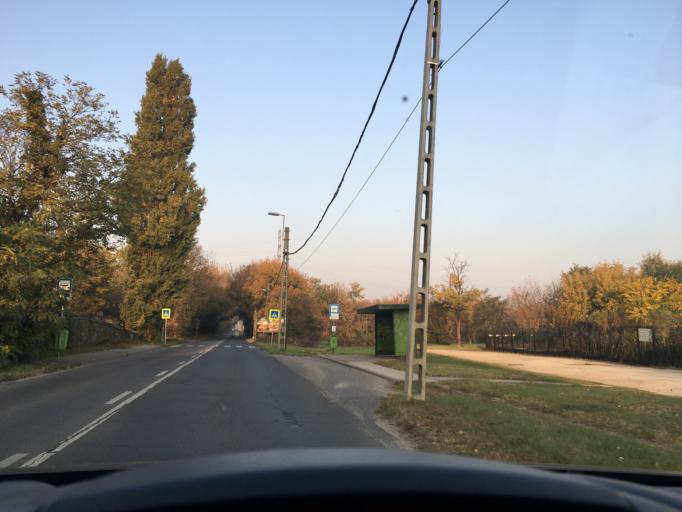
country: HU
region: Budapest
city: Budapest X. keruelet
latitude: 47.4882
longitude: 19.1842
